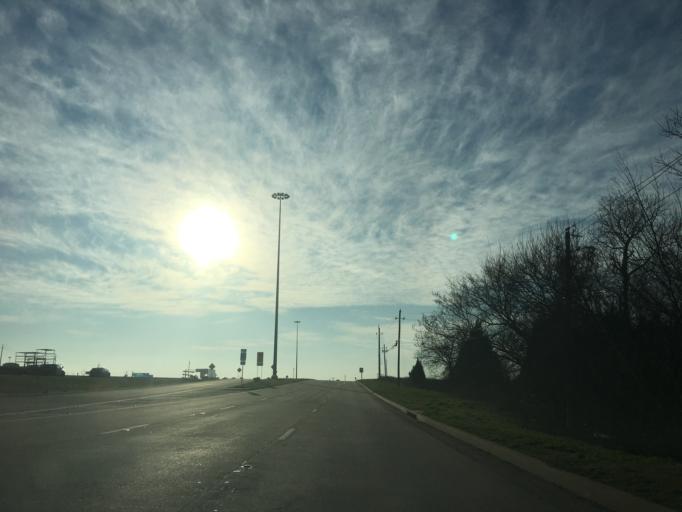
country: US
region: Texas
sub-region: Denton County
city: The Colony
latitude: 33.0849
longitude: -96.8471
